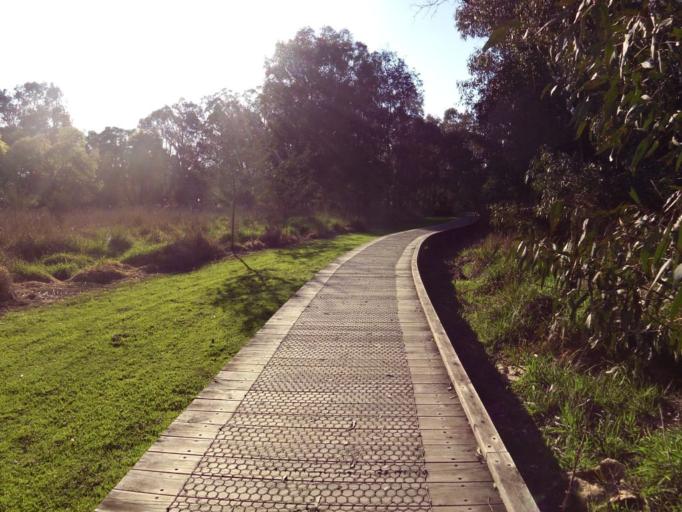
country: AU
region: Victoria
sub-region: Murrindindi
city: Alexandra
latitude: -37.2075
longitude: 145.4275
